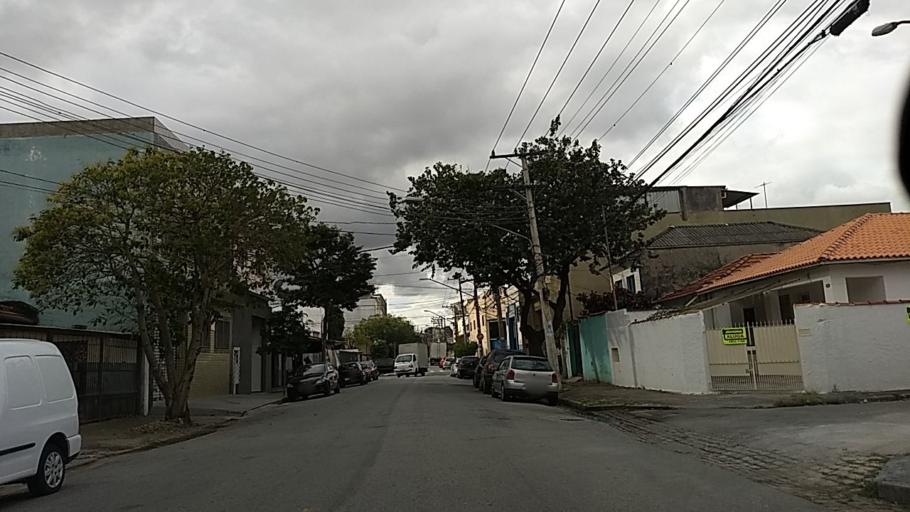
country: BR
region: Sao Paulo
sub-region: Sao Paulo
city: Sao Paulo
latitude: -23.5159
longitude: -46.6107
